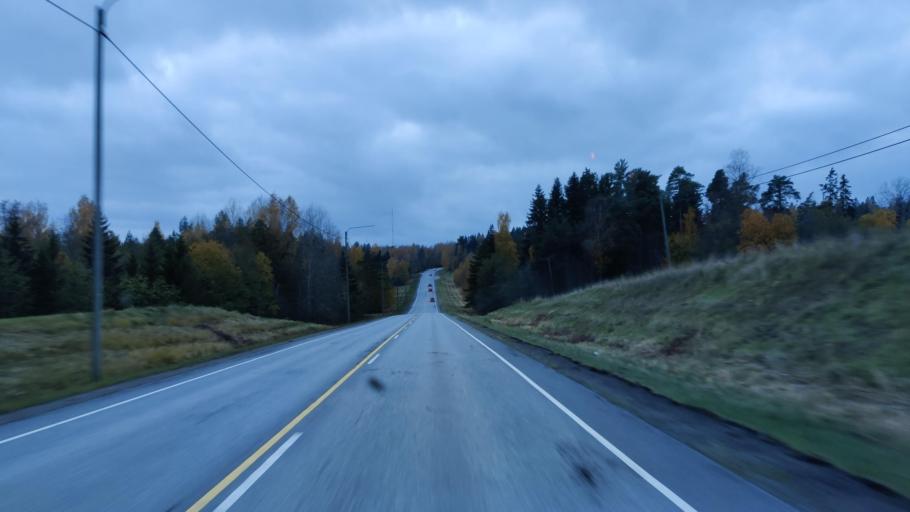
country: FI
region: Uusimaa
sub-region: Helsinki
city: Lohja
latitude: 60.3707
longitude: 24.1340
